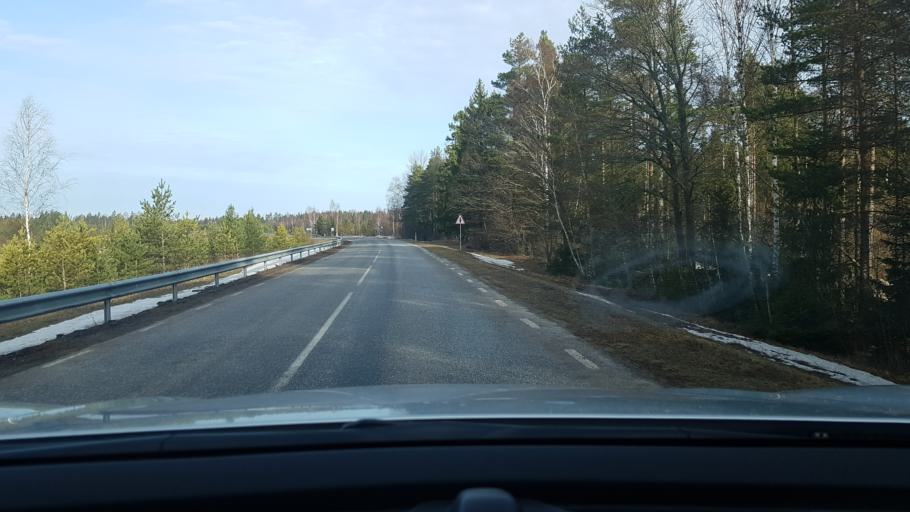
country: EE
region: Saare
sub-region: Kuressaare linn
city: Kuressaare
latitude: 58.4549
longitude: 22.7080
